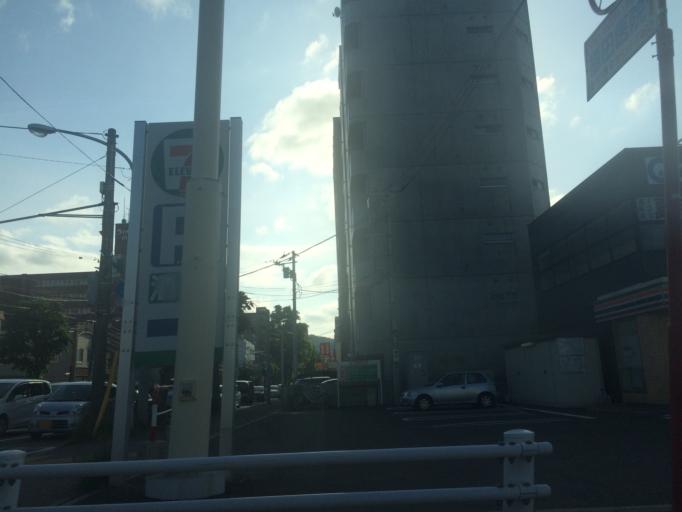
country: JP
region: Hokkaido
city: Sapporo
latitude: 43.0347
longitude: 141.3515
